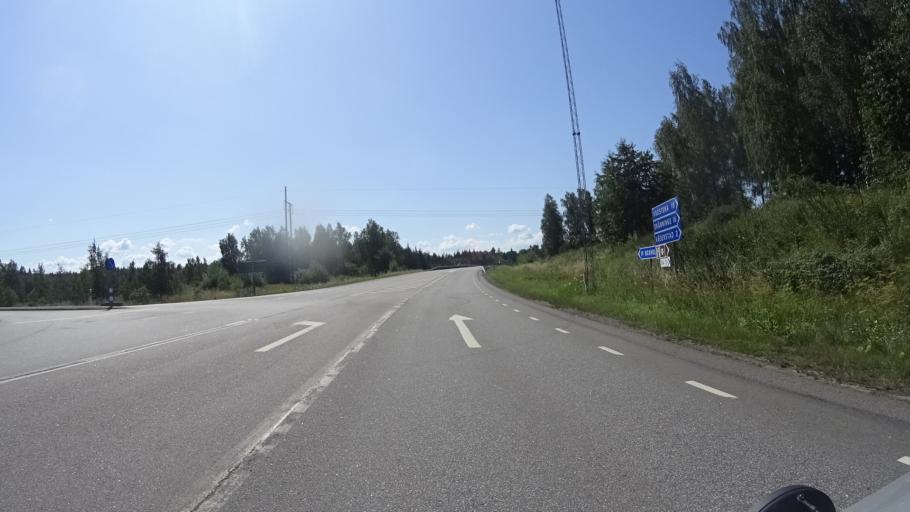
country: SE
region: OEstergoetland
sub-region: Vadstena Kommun
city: Herrestad
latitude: 58.2969
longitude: 14.9225
